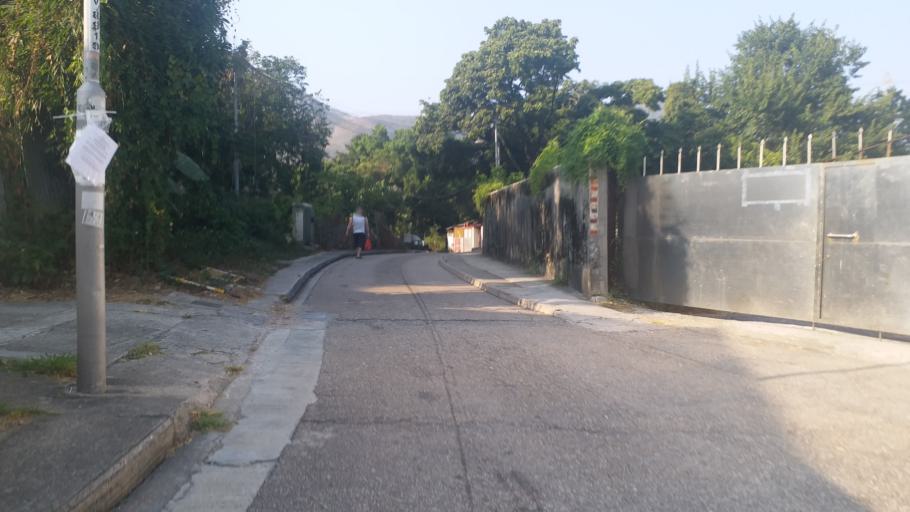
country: HK
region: Tuen Mun
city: Tuen Mun
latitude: 22.4162
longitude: 113.9741
